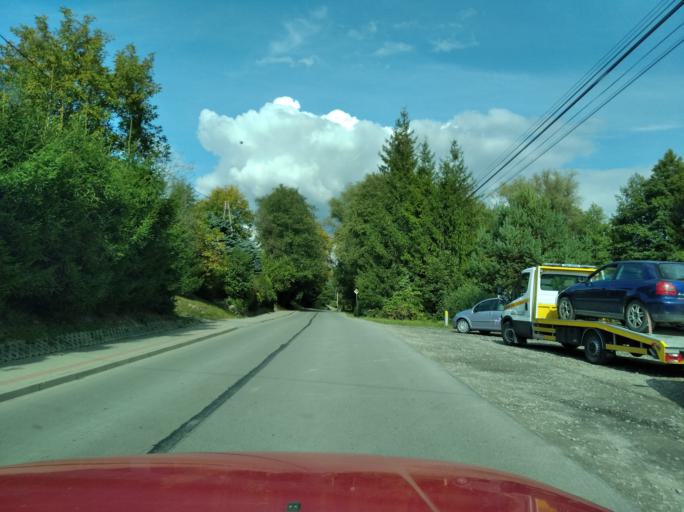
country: PL
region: Subcarpathian Voivodeship
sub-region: Powiat rzeszowski
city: Tyczyn
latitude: 49.9430
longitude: 22.0209
